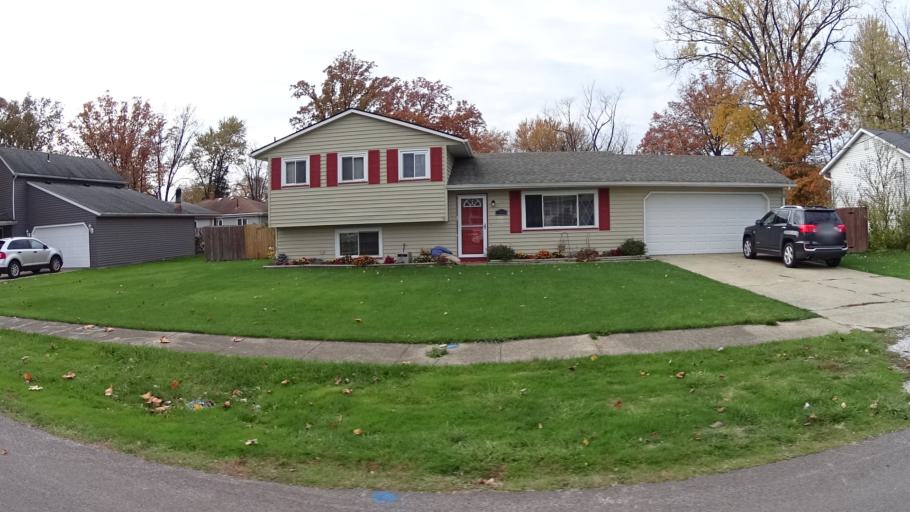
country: US
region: Ohio
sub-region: Lorain County
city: Sheffield Lake
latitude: 41.4871
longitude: -82.0985
